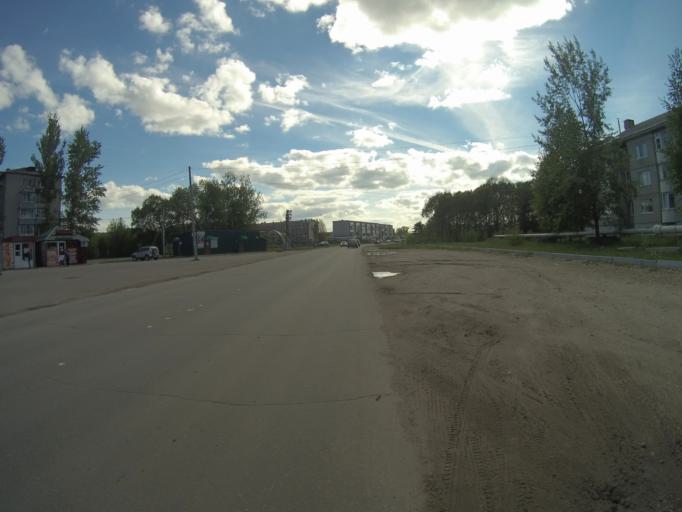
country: RU
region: Vladimir
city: Sudogda
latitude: 55.9535
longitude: 40.8831
